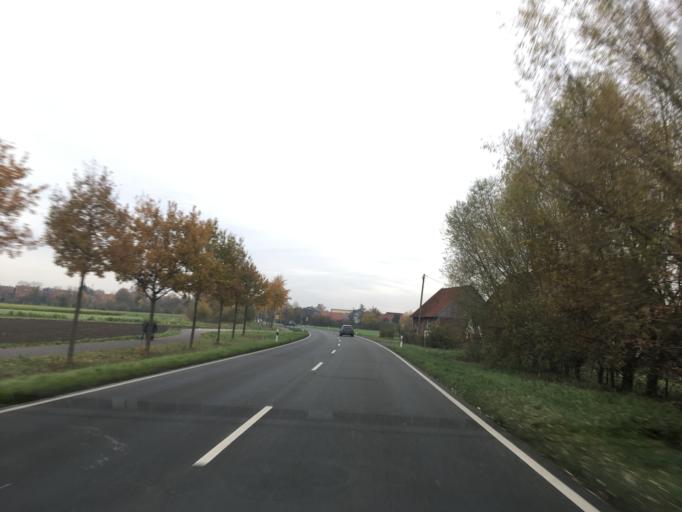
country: DE
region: North Rhine-Westphalia
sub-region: Regierungsbezirk Munster
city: Telgte
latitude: 51.9707
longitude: 7.7766
